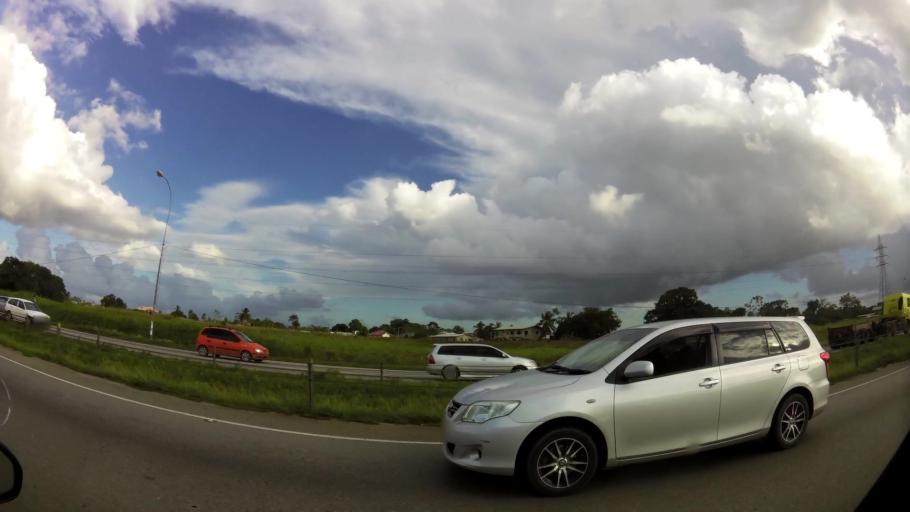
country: TT
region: Chaguanas
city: Chaguanas
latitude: 10.4668
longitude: -61.4084
